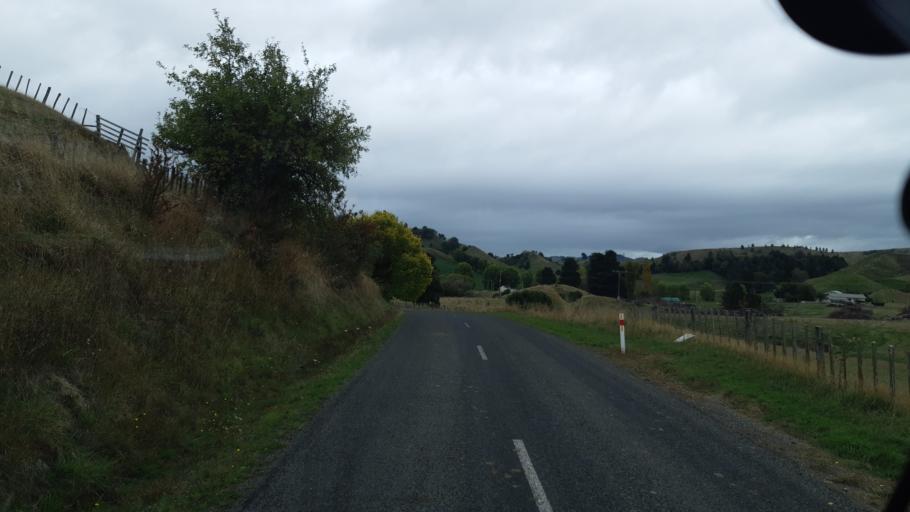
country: NZ
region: Manawatu-Wanganui
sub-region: Ruapehu District
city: Waiouru
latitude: -39.5553
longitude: 175.5846
